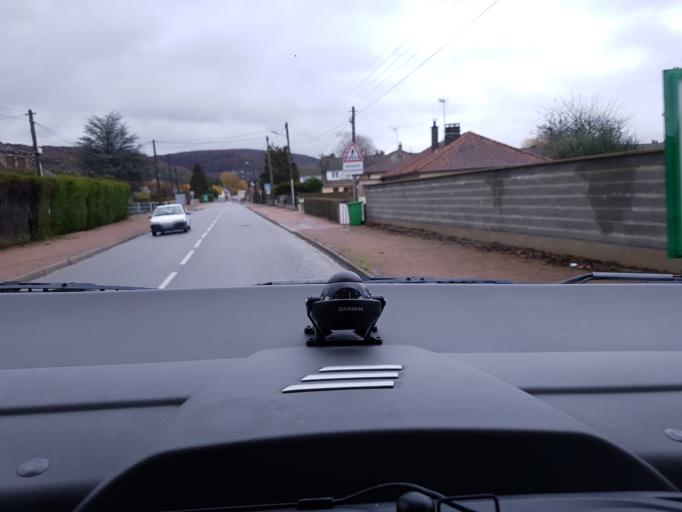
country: FR
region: Haute-Normandie
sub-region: Departement de l'Eure
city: Romilly-sur-Andelle
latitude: 49.3309
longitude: 1.2468
